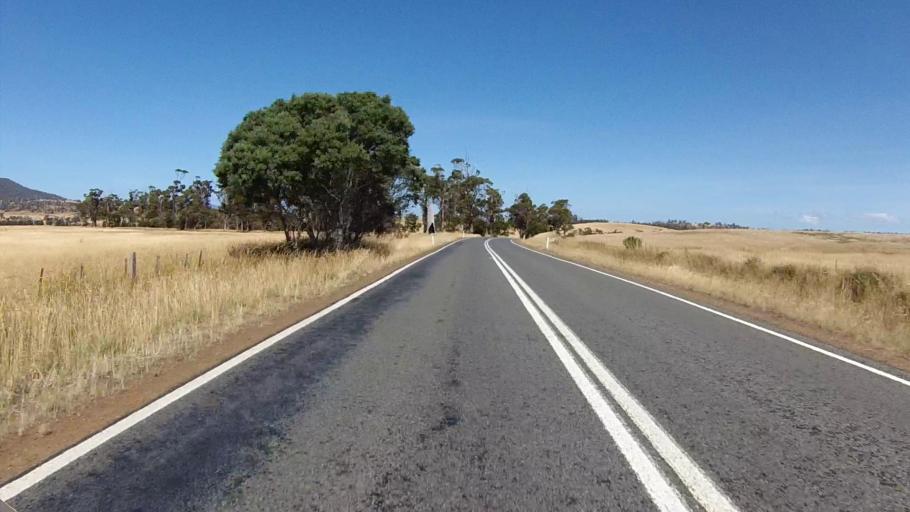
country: AU
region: Tasmania
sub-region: Sorell
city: Sorell
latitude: -42.4505
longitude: 147.9300
